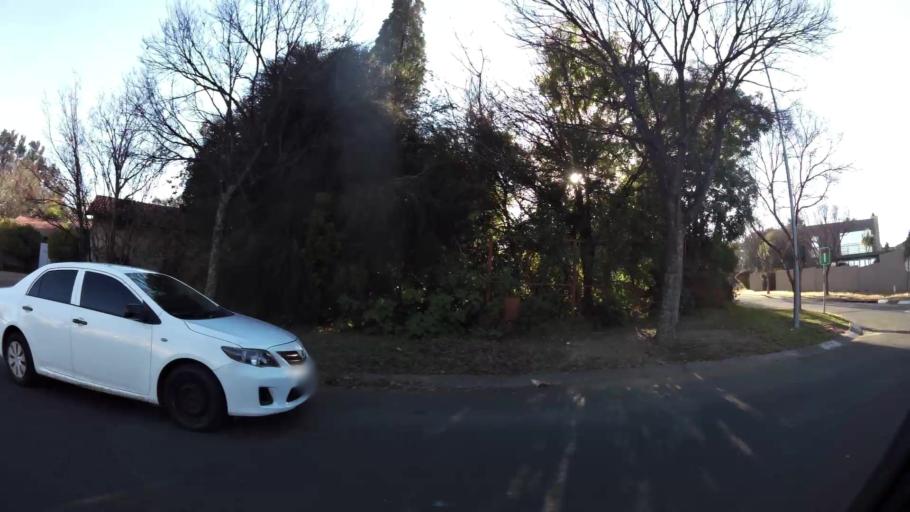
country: ZA
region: Gauteng
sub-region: City of Johannesburg Metropolitan Municipality
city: Midrand
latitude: -26.0352
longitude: 28.0788
